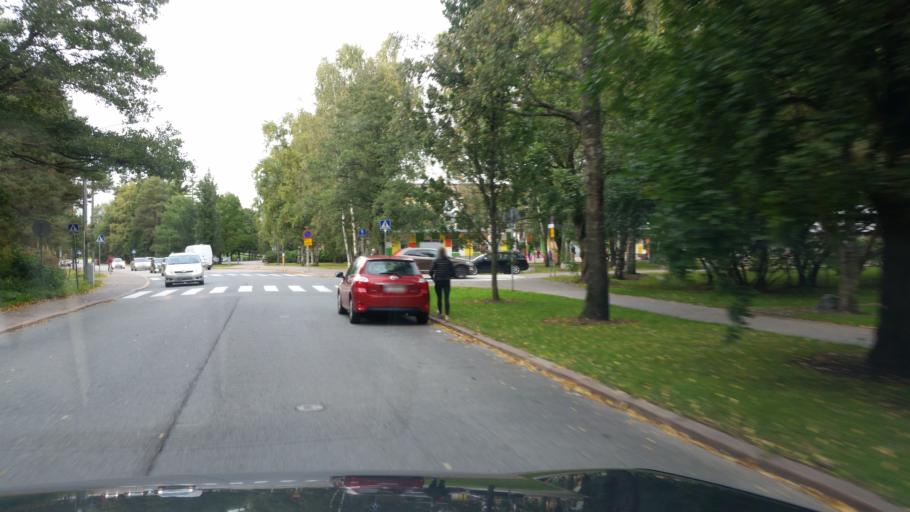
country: FI
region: Uusimaa
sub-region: Helsinki
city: Teekkarikylae
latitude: 60.1544
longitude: 24.8762
